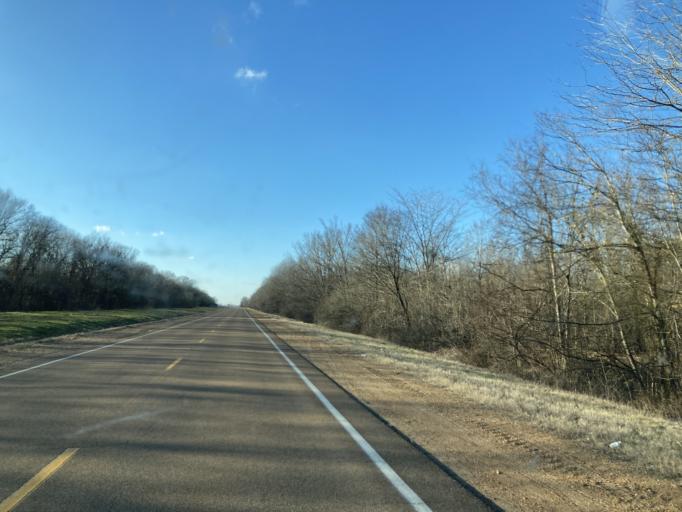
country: US
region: Mississippi
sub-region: Yazoo County
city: Yazoo City
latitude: 32.9203
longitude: -90.5609
